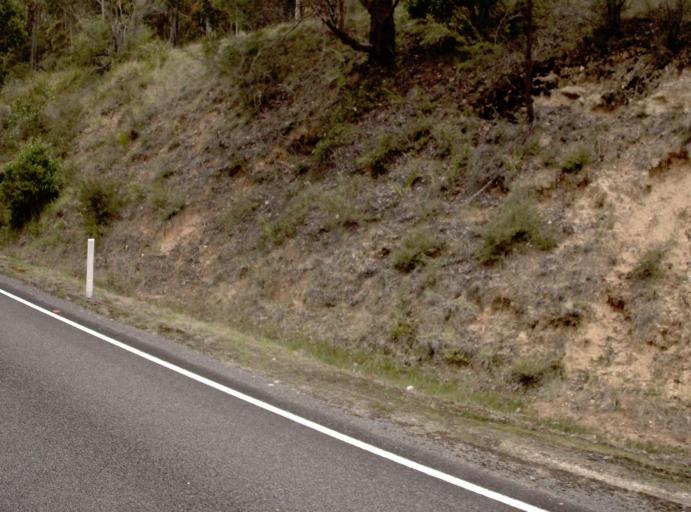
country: AU
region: New South Wales
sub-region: Bombala
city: Bombala
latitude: -37.2320
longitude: 149.2728
